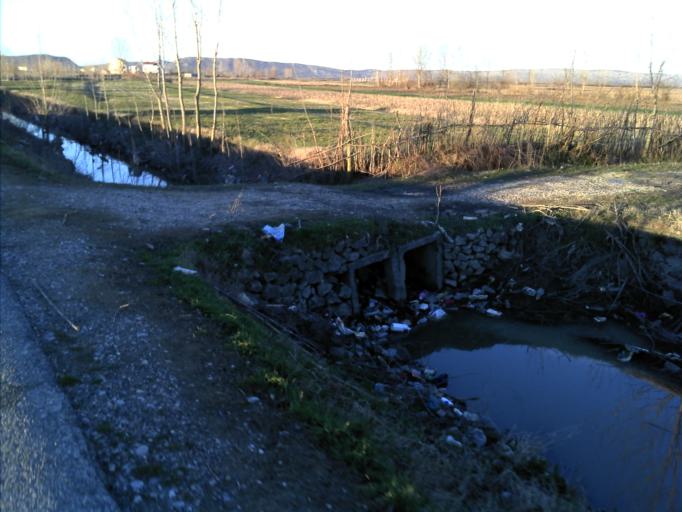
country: AL
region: Shkoder
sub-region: Rrethi i Shkodres
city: Berdica e Madhe
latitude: 41.9651
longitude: 19.4733
